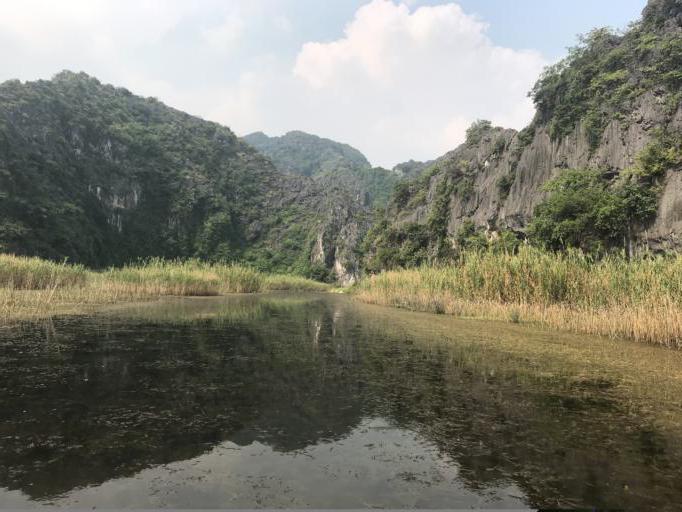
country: VN
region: Ninh Binh
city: Thi Tran Me
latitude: 20.3646
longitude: 105.8898
